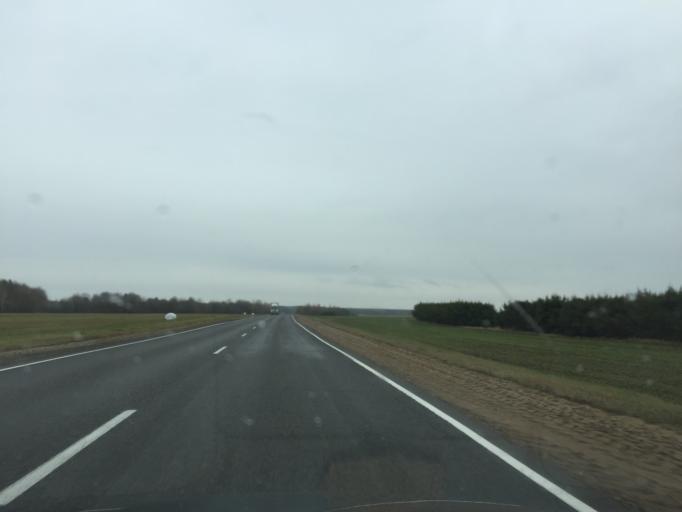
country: BY
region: Mogilev
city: Cherykaw
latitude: 53.5911
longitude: 31.3717
